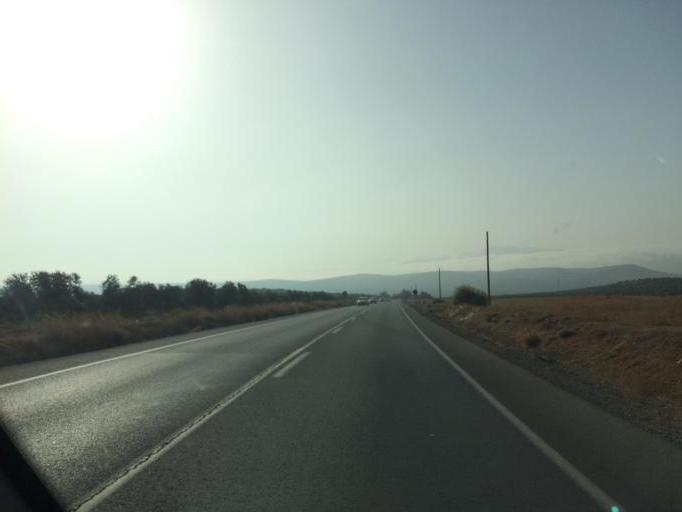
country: ES
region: Andalusia
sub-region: Provincia de Malaga
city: Campillos
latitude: 37.0532
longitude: -4.7806
